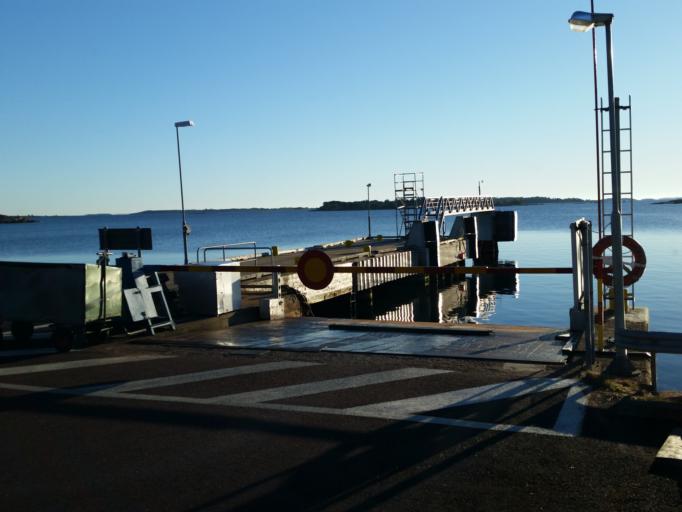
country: AX
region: Alands skaergard
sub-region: Vardoe
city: Vardoe
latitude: 60.2242
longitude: 20.4133
